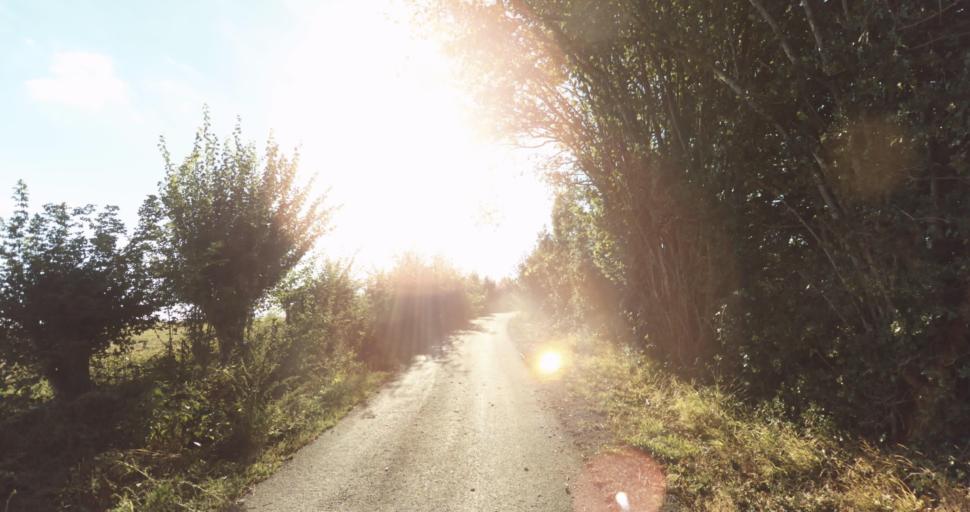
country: FR
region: Lower Normandy
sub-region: Departement de l'Orne
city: Vimoutiers
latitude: 48.8898
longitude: 0.1288
